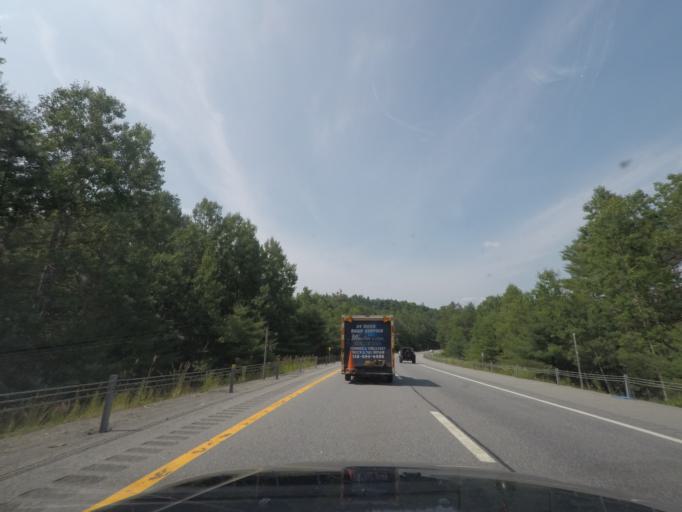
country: US
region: New York
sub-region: Warren County
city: Warrensburg
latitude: 43.6465
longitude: -73.7640
